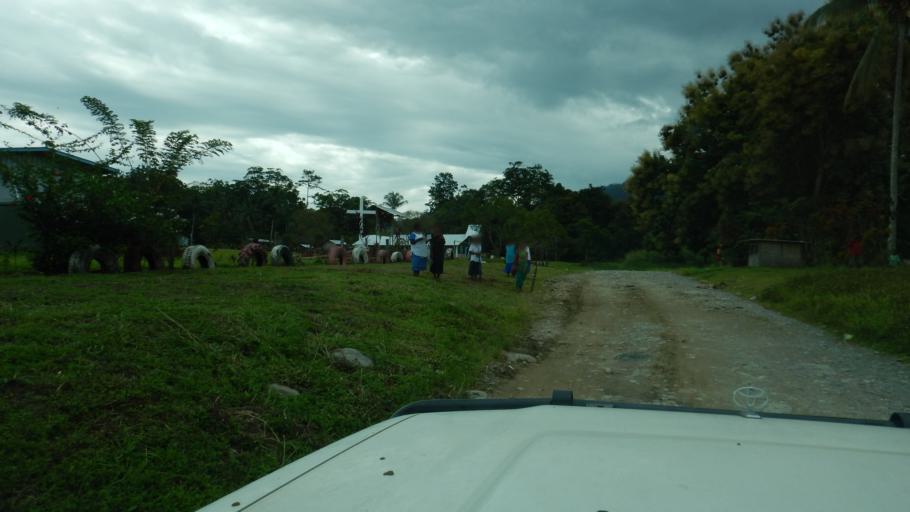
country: PG
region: Northern Province
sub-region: Sohe
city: Kokoda
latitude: -8.9174
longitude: 147.8780
